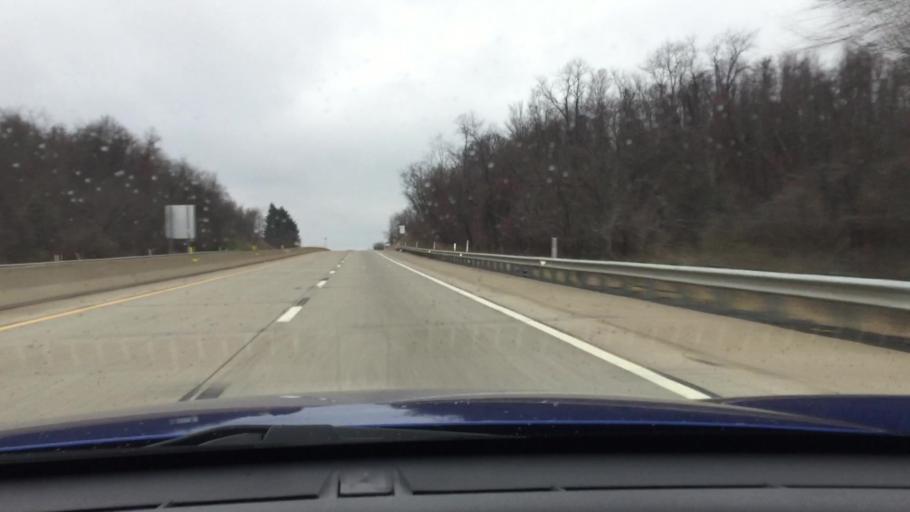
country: US
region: Pennsylvania
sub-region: Allegheny County
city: Imperial
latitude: 40.4368
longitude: -80.2484
